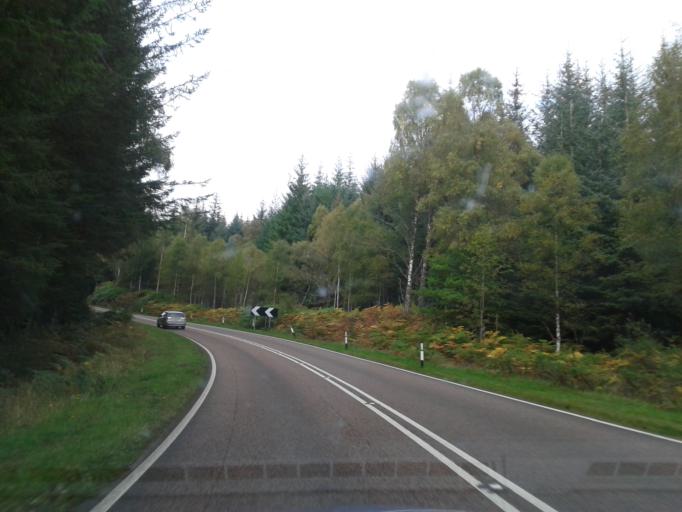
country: GB
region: Scotland
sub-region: Highland
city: Spean Bridge
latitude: 57.0748
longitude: -4.8353
